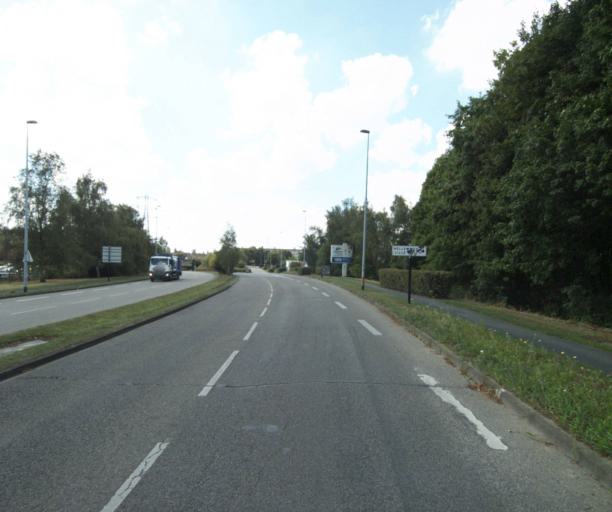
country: FR
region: Nord-Pas-de-Calais
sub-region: Departement du Nord
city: Mons-en-Baroeul
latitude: 50.6264
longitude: 3.1209
